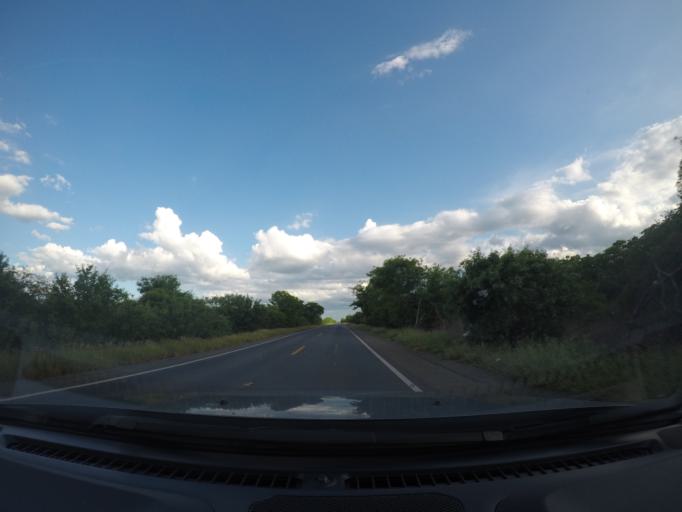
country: BR
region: Bahia
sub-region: Oliveira Dos Brejinhos
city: Beira Rio
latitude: -12.2205
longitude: -42.7920
